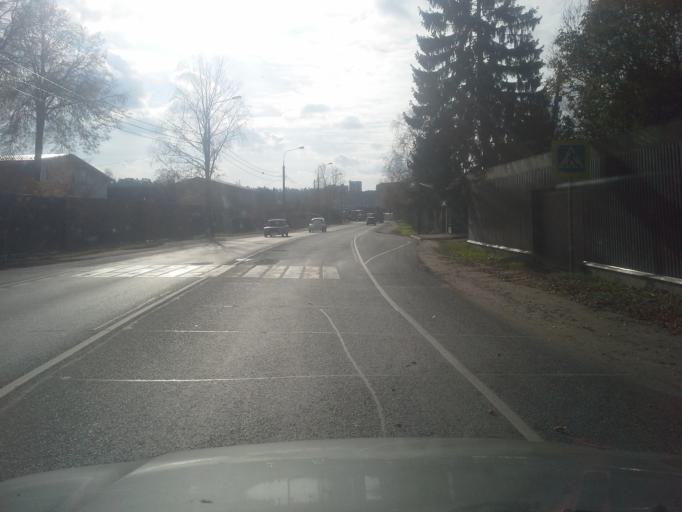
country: RU
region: Moskovskaya
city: Zvenigorod
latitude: 55.7170
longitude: 36.8662
